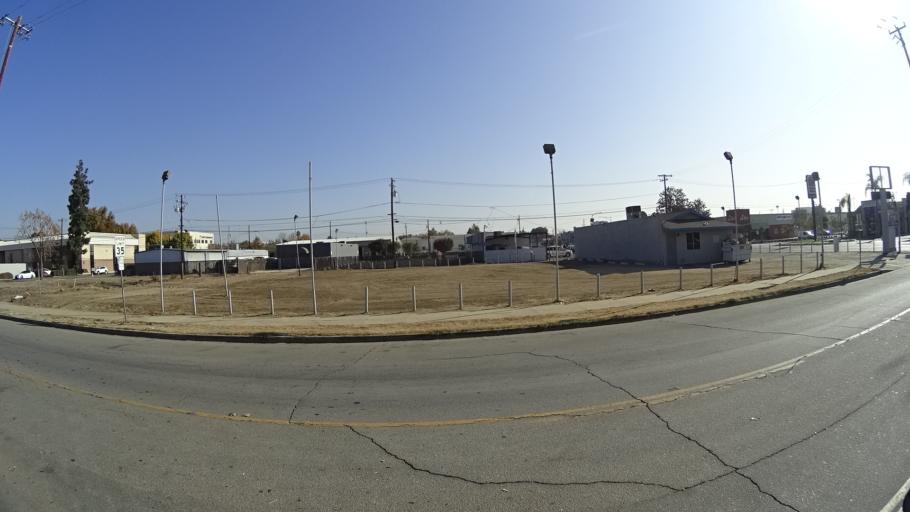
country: US
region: California
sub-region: Kern County
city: Bakersfield
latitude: 35.3814
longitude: -119.0213
